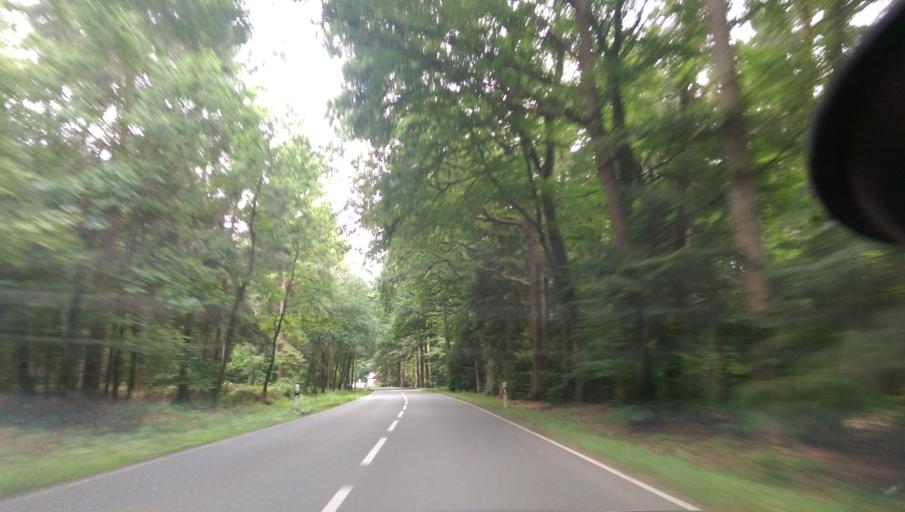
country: DE
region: Lower Saxony
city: Bomlitz
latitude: 52.9555
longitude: 9.6583
